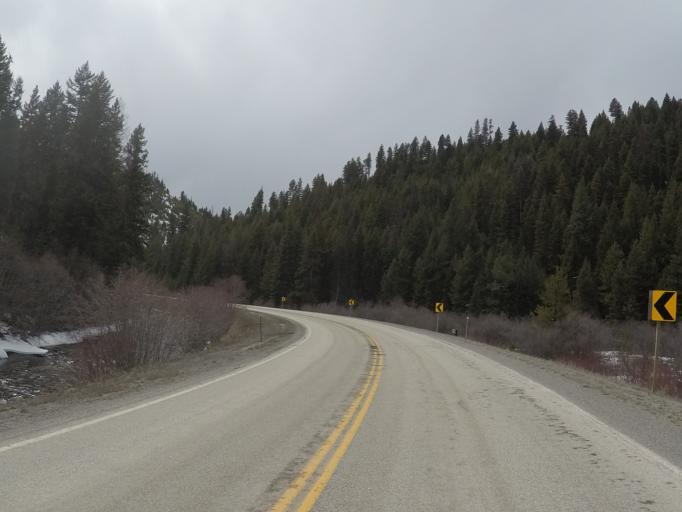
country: US
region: Montana
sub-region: Missoula County
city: Frenchtown
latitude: 46.7561
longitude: -114.4980
